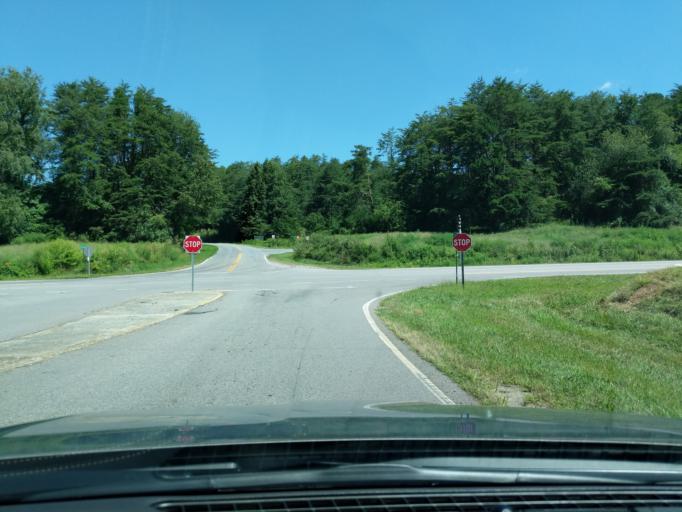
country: US
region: North Carolina
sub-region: Clay County
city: Hayesville
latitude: 35.0324
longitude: -83.7339
